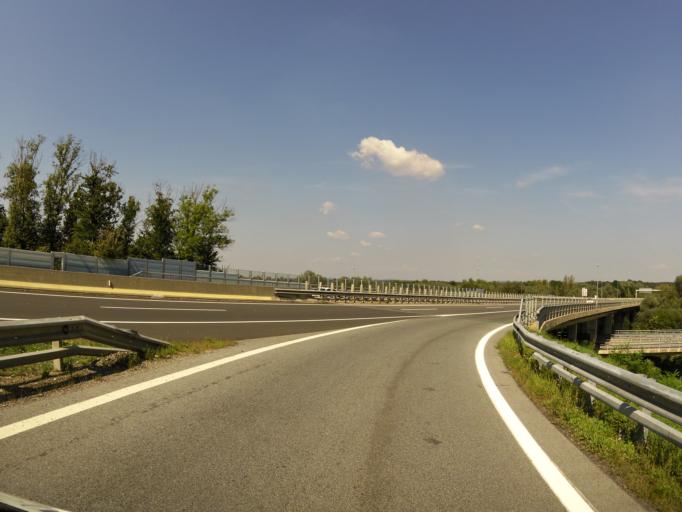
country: AT
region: Styria
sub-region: Politischer Bezirk Leibnitz
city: Spielfeld
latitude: 46.7051
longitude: 15.6397
